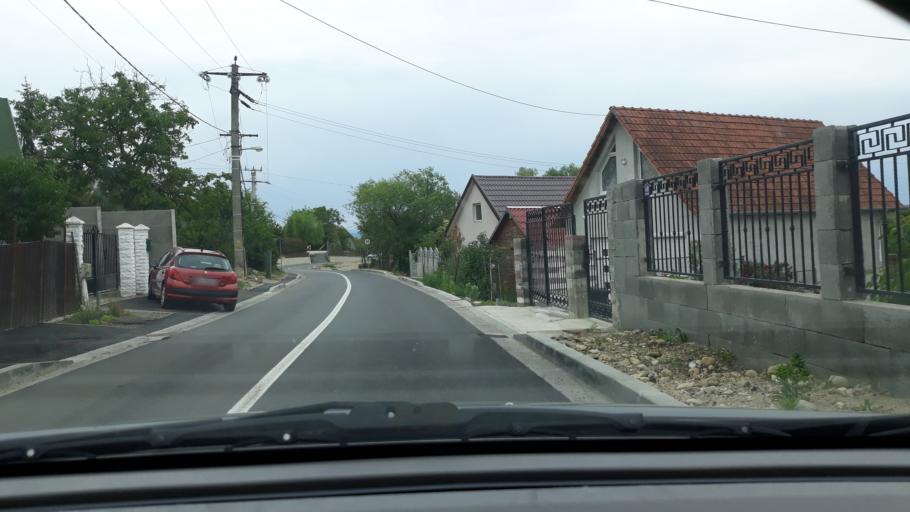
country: RO
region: Bihor
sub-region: Comuna Osorheiu
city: Osorheiu
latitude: 47.0590
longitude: 22.0170
